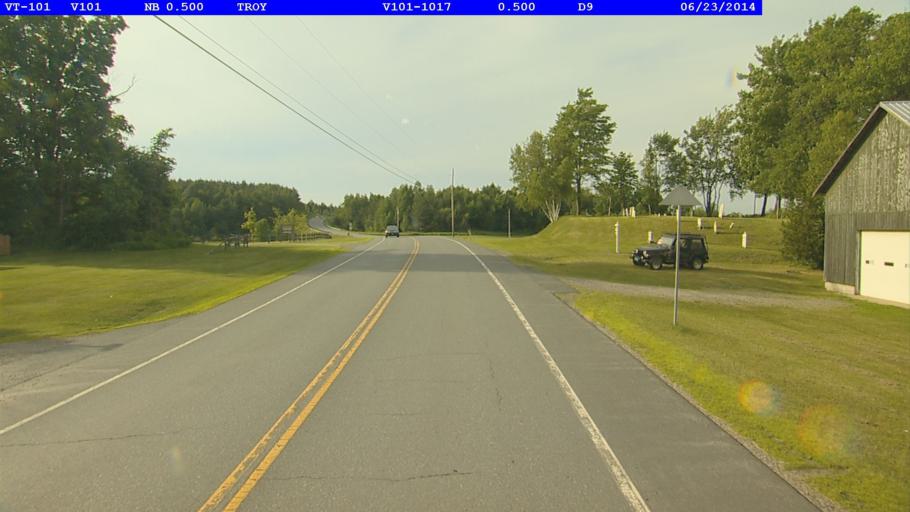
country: US
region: Vermont
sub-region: Orleans County
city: Newport
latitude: 44.9108
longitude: -72.4054
